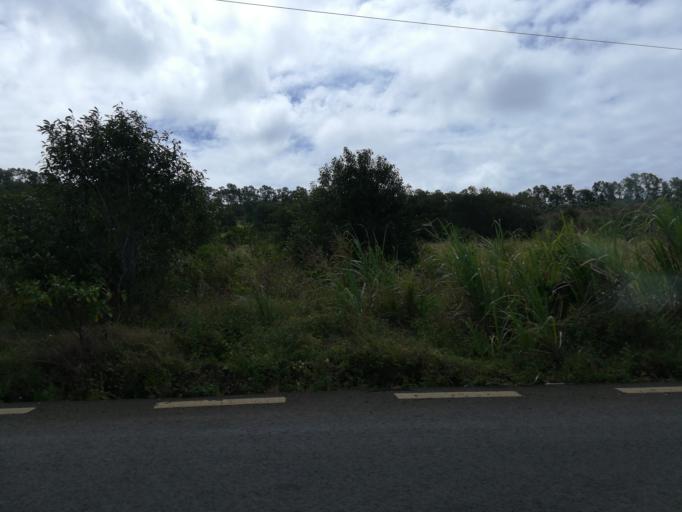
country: MU
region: Grand Port
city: Bambous Virieux
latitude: -20.3364
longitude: 57.7624
